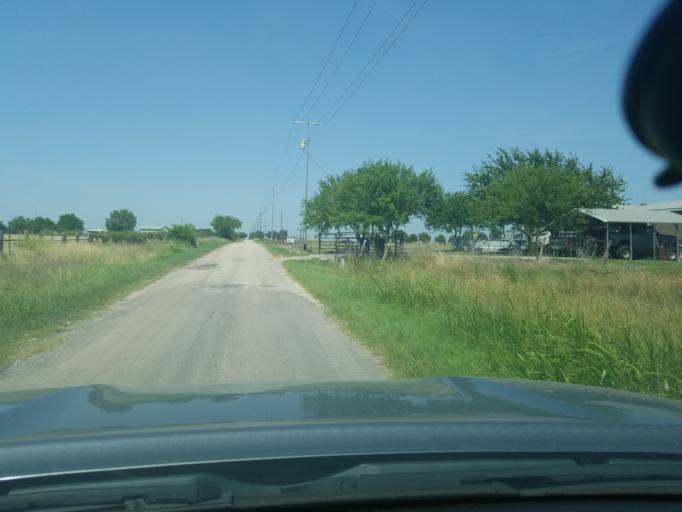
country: US
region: Texas
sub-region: Guadalupe County
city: Lake Dunlap
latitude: 29.6730
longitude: -98.0515
